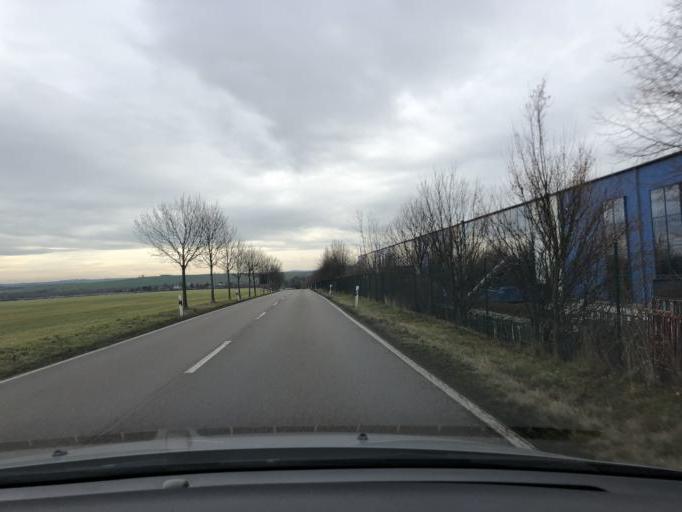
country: DE
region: Saxony
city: Nossen
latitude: 51.0665
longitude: 13.3394
